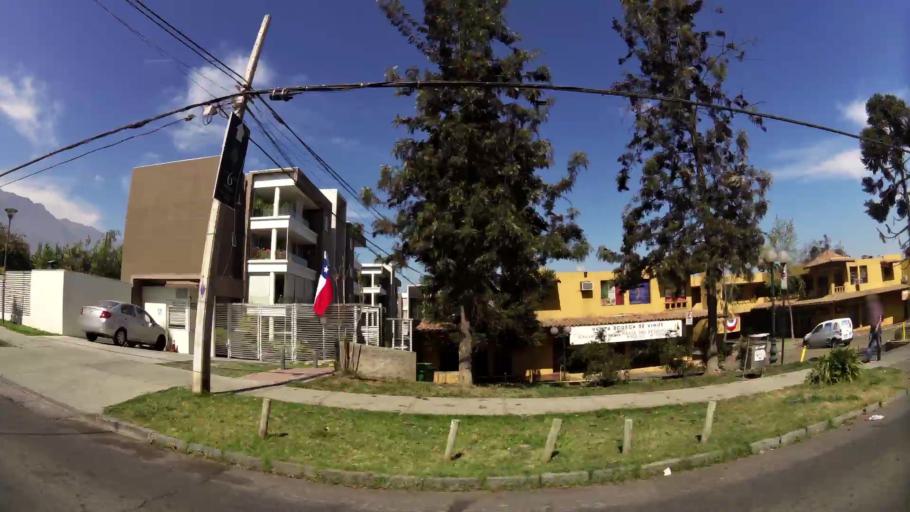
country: CL
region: Santiago Metropolitan
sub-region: Provincia de Santiago
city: Villa Presidente Frei, Nunoa, Santiago, Chile
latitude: -33.4408
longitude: -70.5332
